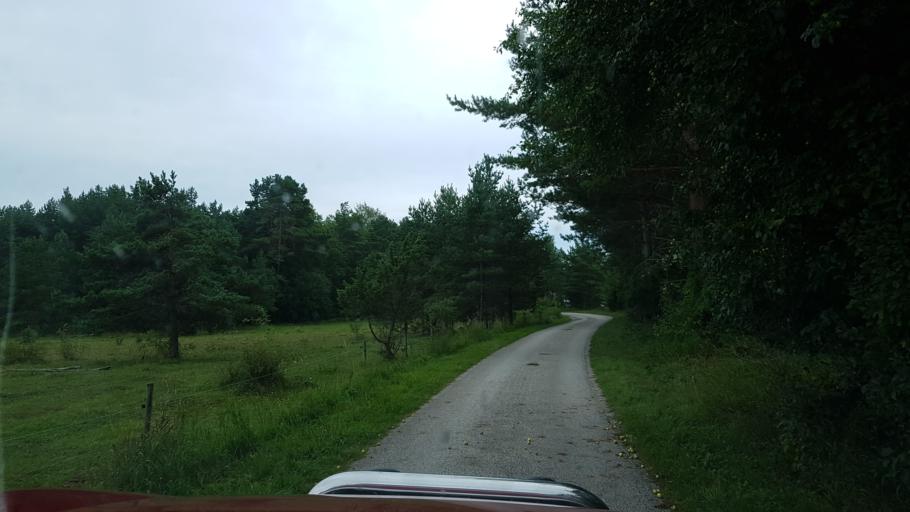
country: EE
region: Laeaene
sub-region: Ridala Parish
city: Uuemoisa
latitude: 58.9998
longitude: 23.6385
